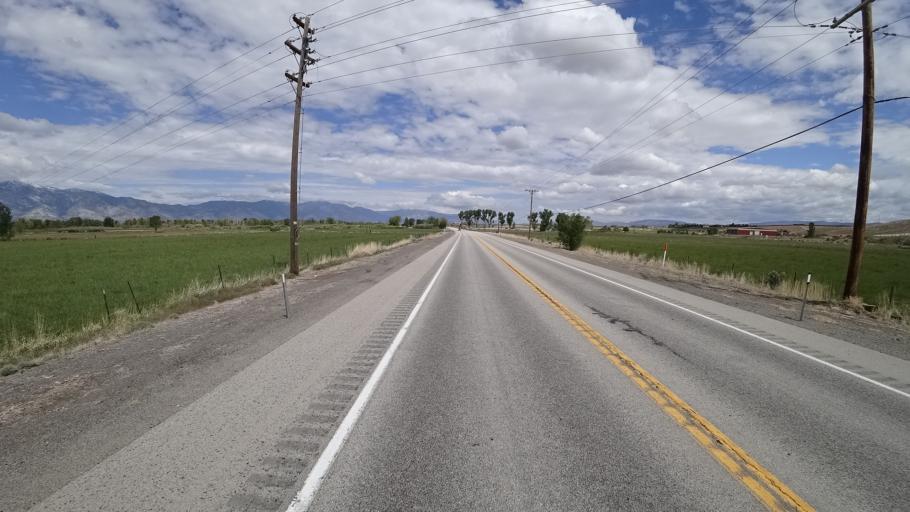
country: US
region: Nevada
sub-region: Douglas County
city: Gardnerville Ranchos
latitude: 38.8960
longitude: -119.7015
